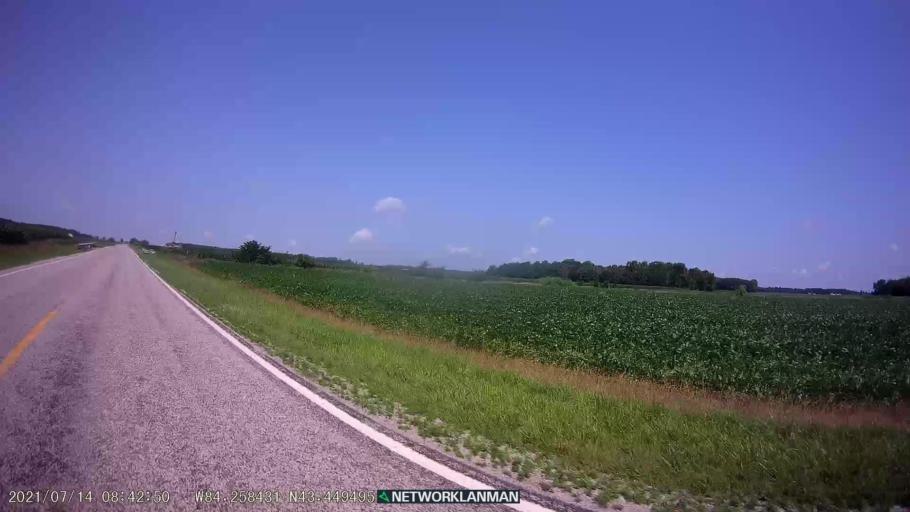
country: US
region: Michigan
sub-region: Saginaw County
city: Hemlock
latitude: 43.4495
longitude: -84.2587
